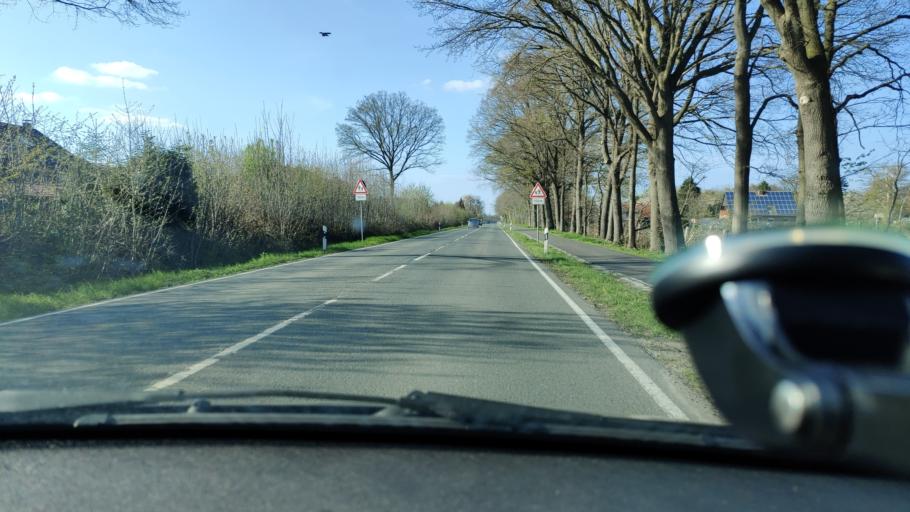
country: DE
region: North Rhine-Westphalia
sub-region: Regierungsbezirk Munster
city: Velen
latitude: 51.8973
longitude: 7.0419
